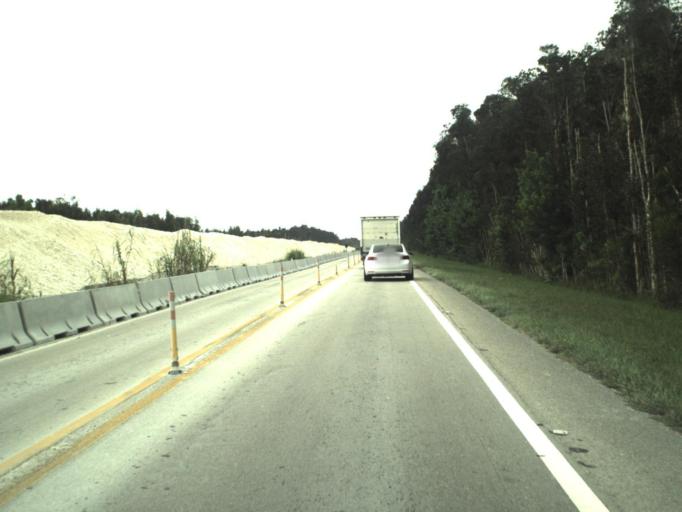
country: US
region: Florida
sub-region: Miami-Dade County
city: Kendall West
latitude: 25.7493
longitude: -80.4810
